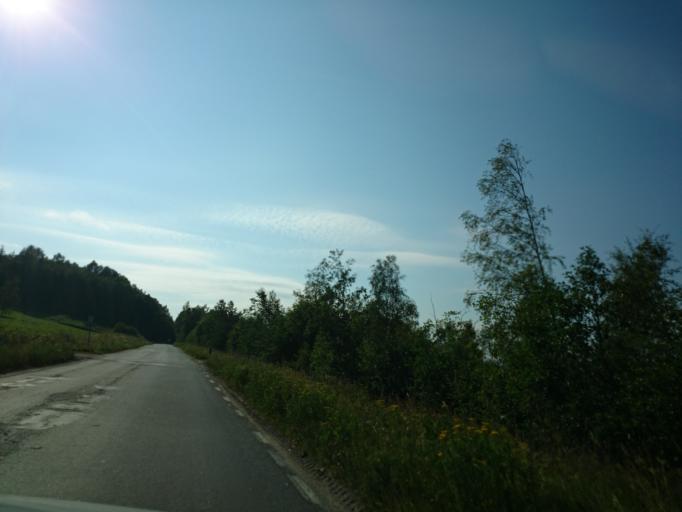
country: SE
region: Vaesternorrland
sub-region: Sundsvalls Kommun
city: Njurundabommen
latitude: 62.2210
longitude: 17.3425
